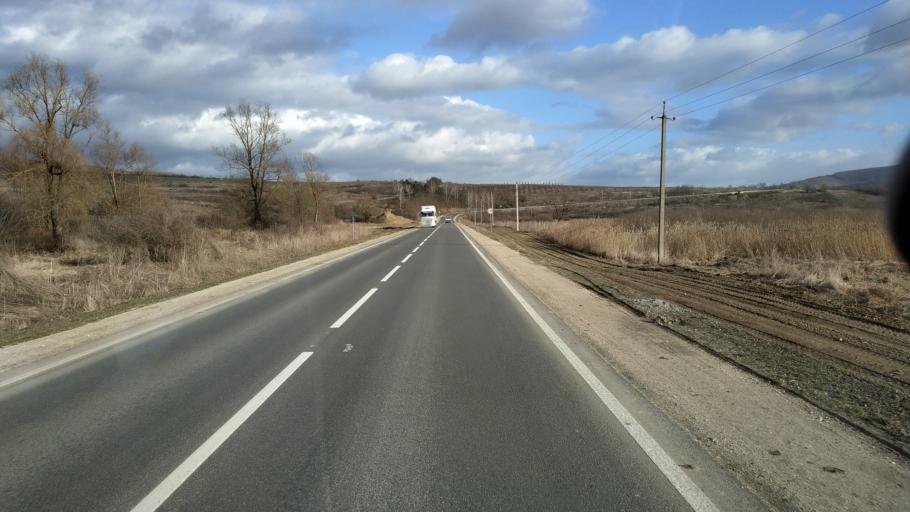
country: MD
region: Calarasi
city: Calarasi
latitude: 47.3012
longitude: 28.1469
